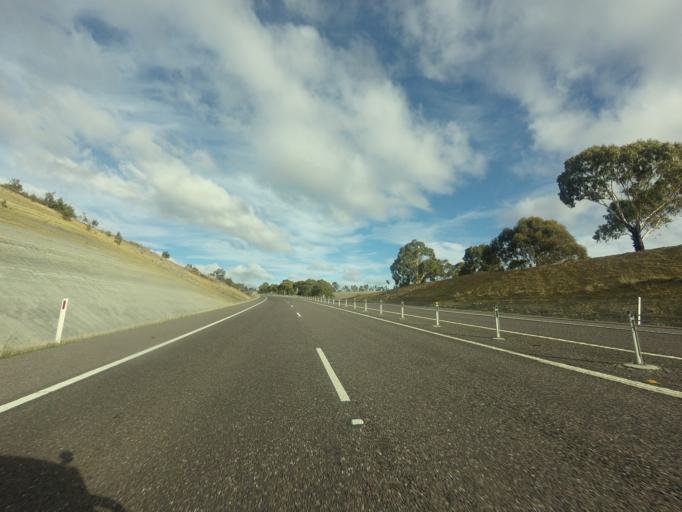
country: AU
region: Tasmania
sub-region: Brighton
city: Bridgewater
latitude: -42.5661
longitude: 147.2090
